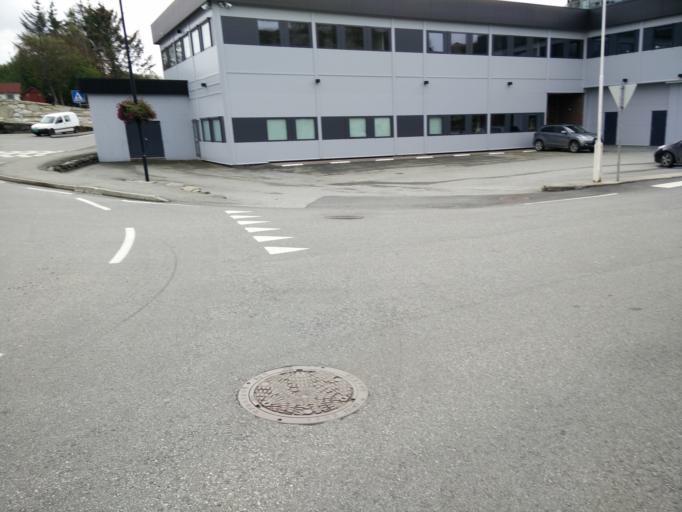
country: NO
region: Hordaland
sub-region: Sveio
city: Sveio
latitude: 59.6022
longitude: 5.2081
